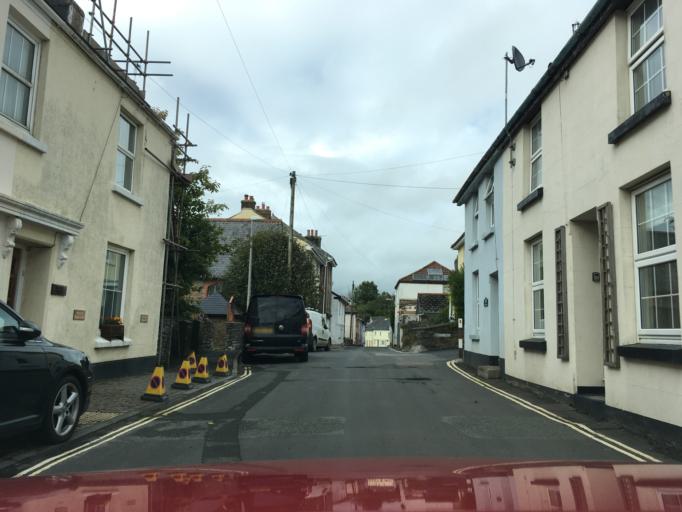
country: GB
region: England
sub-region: Devon
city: Modbury
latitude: 50.3128
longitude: -3.8365
